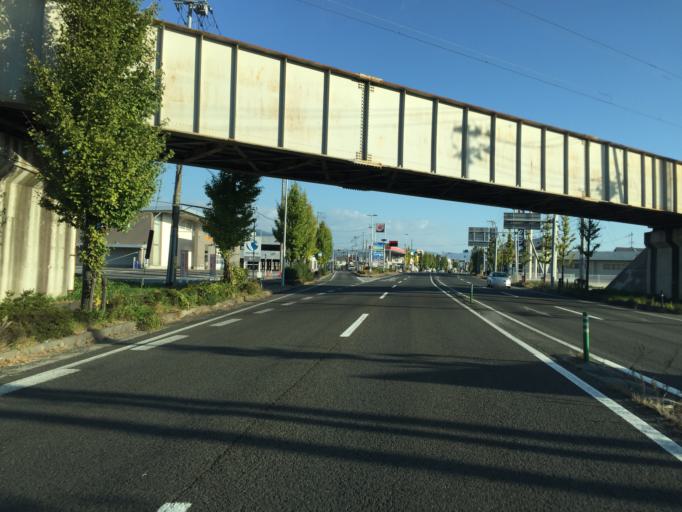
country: JP
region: Fukushima
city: Fukushima-shi
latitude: 37.7991
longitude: 140.4902
